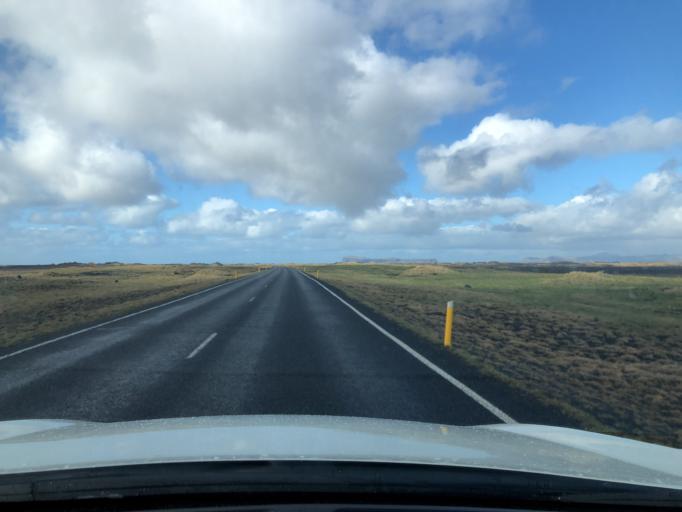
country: IS
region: South
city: Vestmannaeyjar
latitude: 63.4941
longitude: -18.5221
